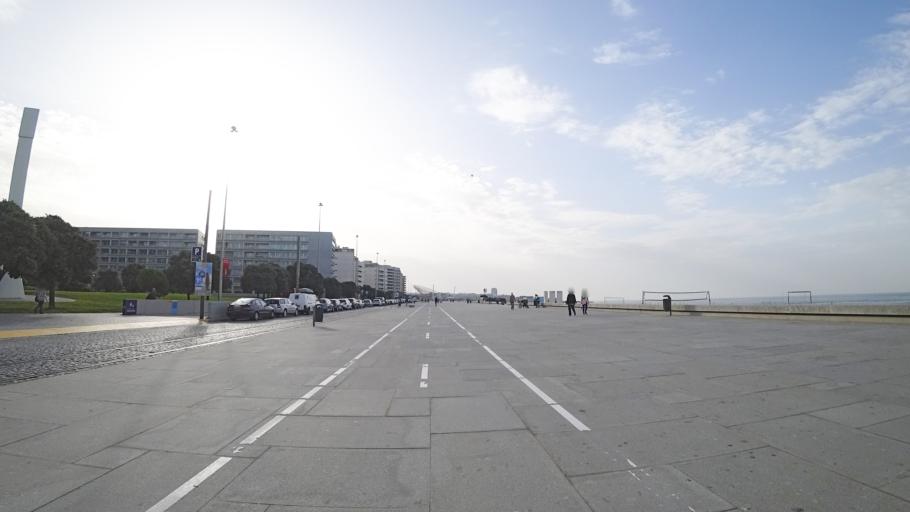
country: PT
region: Porto
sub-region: Matosinhos
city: Matosinhos
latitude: 41.1788
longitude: -8.6931
